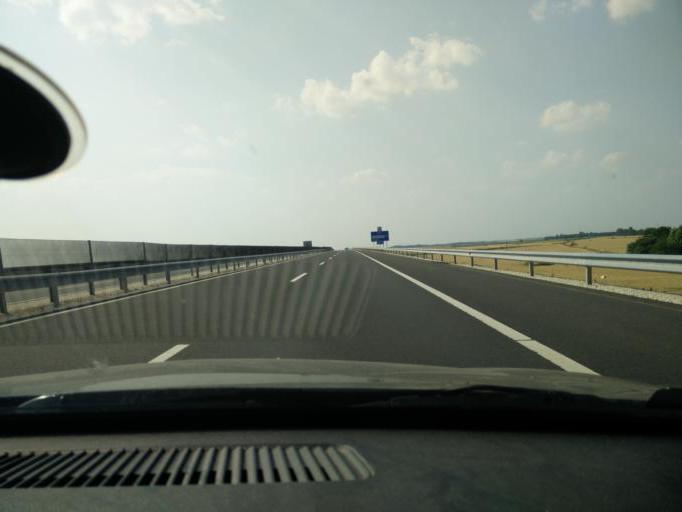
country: HU
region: Tolna
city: Tolna
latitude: 46.4005
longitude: 18.7476
